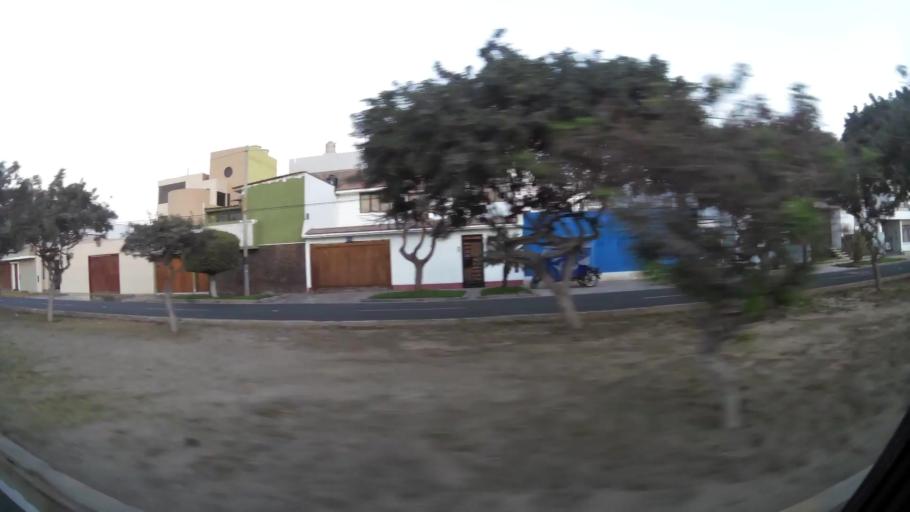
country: PE
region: Ancash
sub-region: Provincia de Santa
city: Buenos Aires
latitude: -9.1252
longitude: -78.5325
